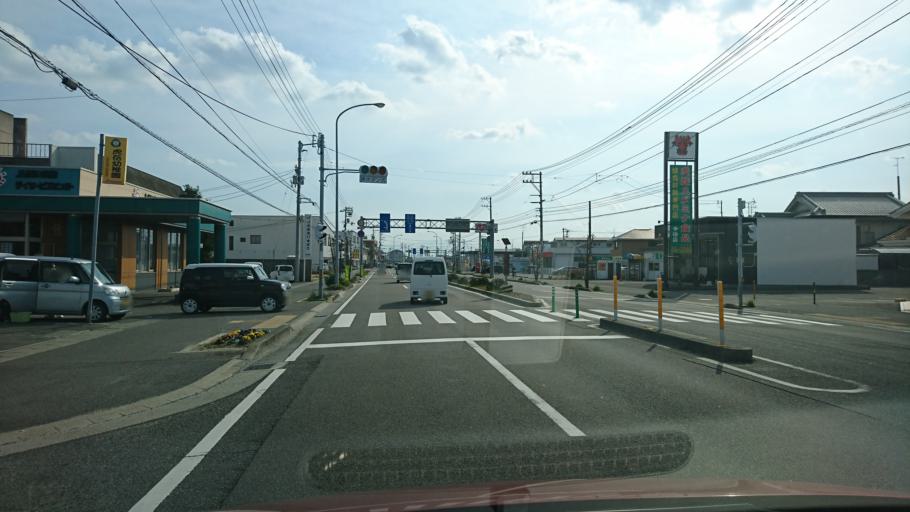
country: JP
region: Ehime
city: Hojo
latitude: 34.0846
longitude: 132.9900
